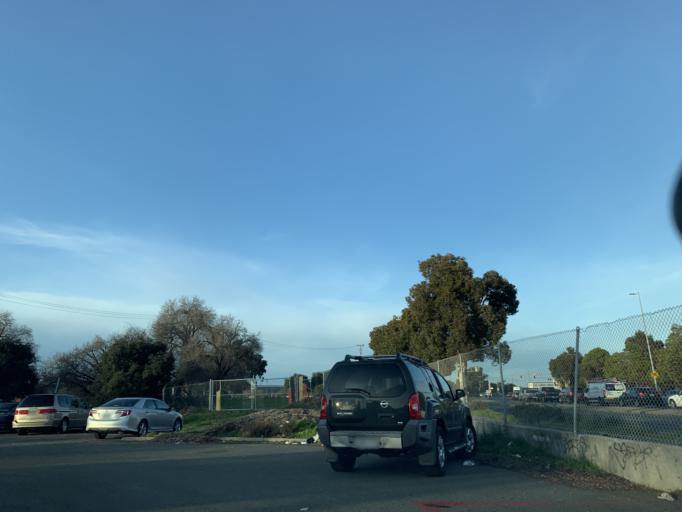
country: US
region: California
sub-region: Contra Costa County
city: North Richmond
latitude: 37.9295
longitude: -122.3786
